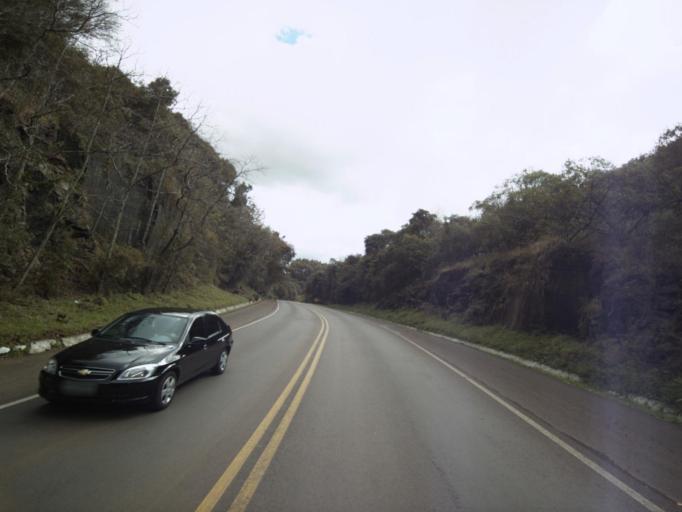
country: BR
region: Santa Catarina
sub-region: Concordia
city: Concordia
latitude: -27.2901
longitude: -51.9677
